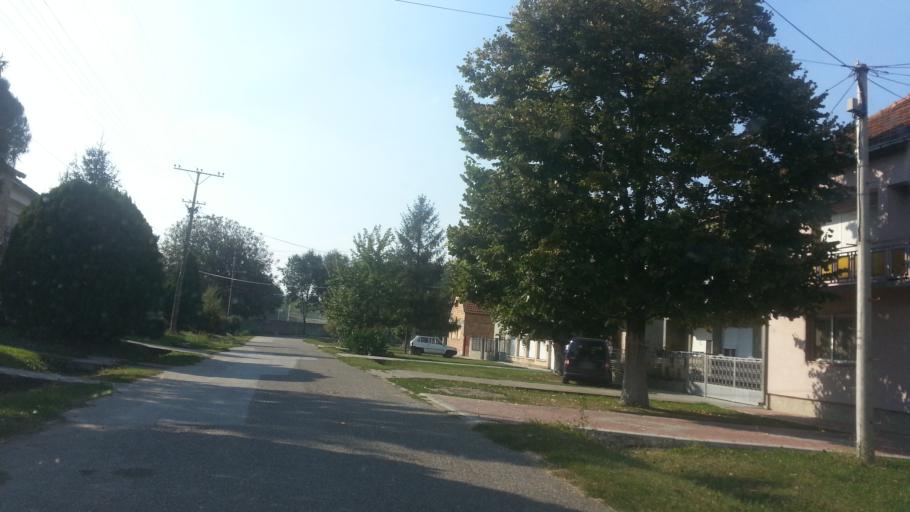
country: RS
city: Stari Banovci
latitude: 44.9887
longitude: 20.2788
